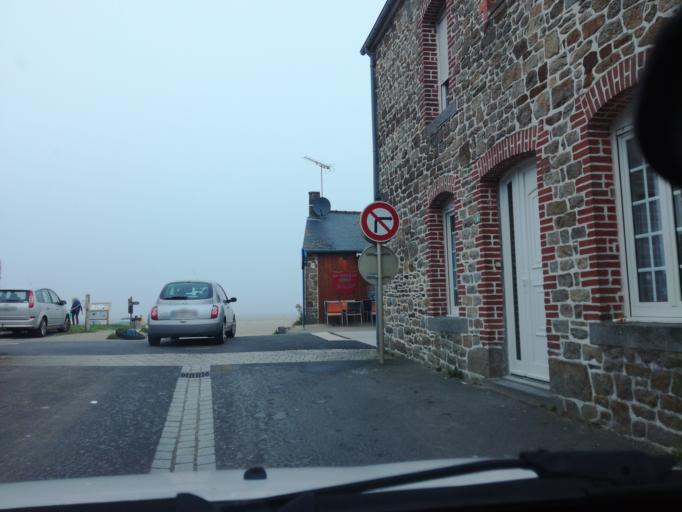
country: FR
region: Brittany
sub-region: Departement d'Ille-et-Vilaine
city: Cherrueix
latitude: 48.6062
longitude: -1.7107
